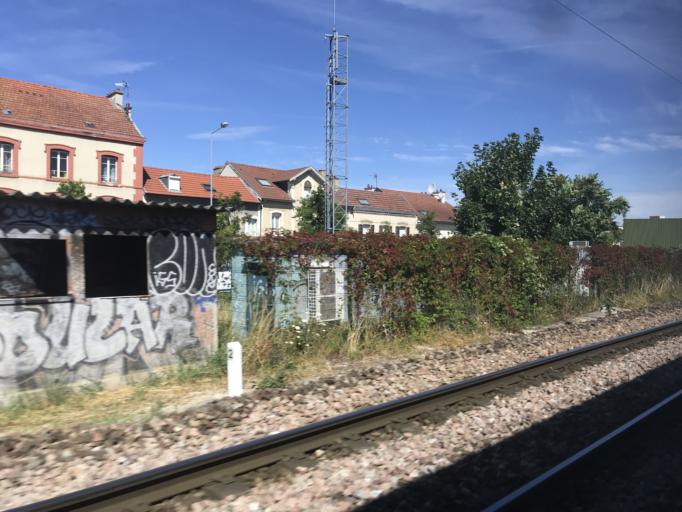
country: FR
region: Champagne-Ardenne
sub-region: Departement de la Marne
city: Reims
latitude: 49.2467
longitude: 4.0126
